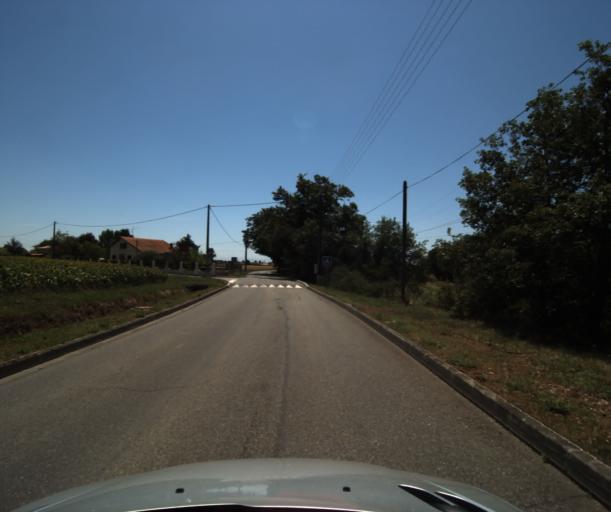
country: FR
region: Midi-Pyrenees
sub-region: Departement de la Haute-Garonne
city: Pinsaguel
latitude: 43.5037
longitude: 1.3786
